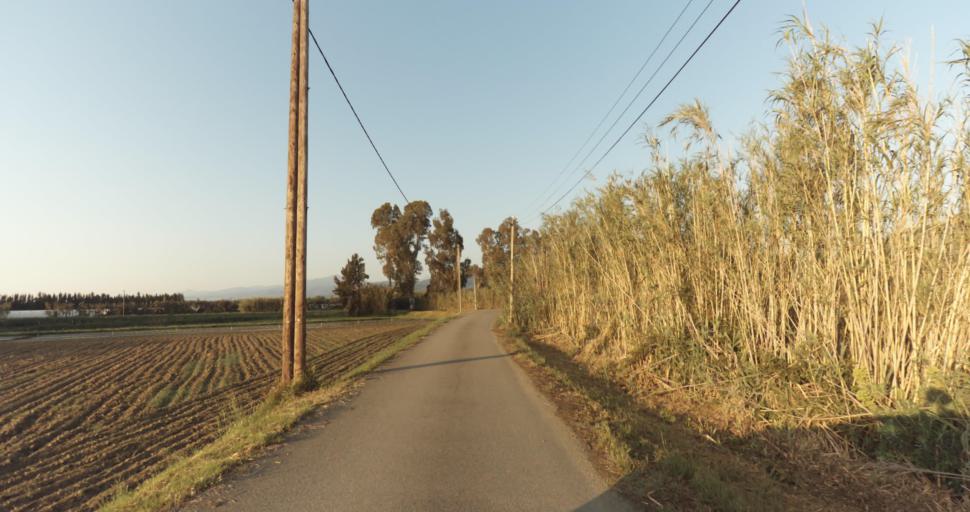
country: FR
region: Corsica
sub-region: Departement de la Haute-Corse
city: Biguglia
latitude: 42.6248
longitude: 9.4515
